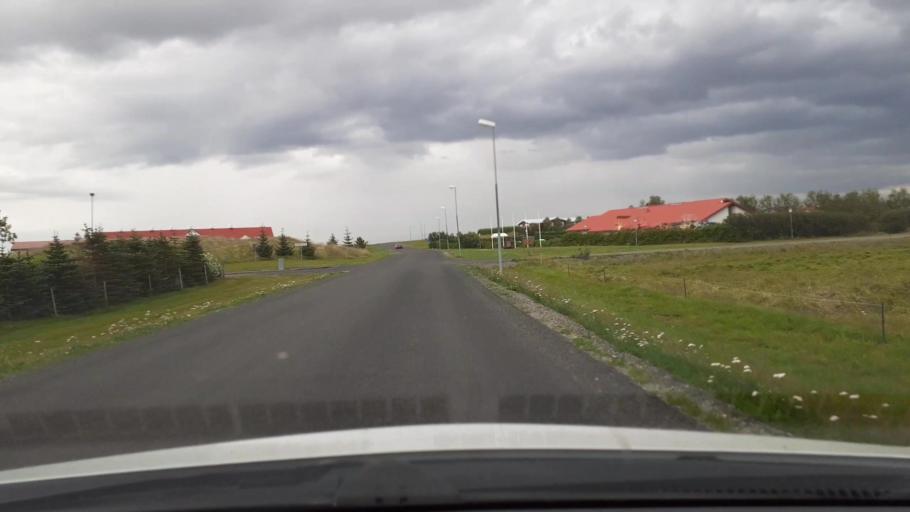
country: IS
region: West
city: Borgarnes
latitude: 64.5638
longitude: -21.7610
